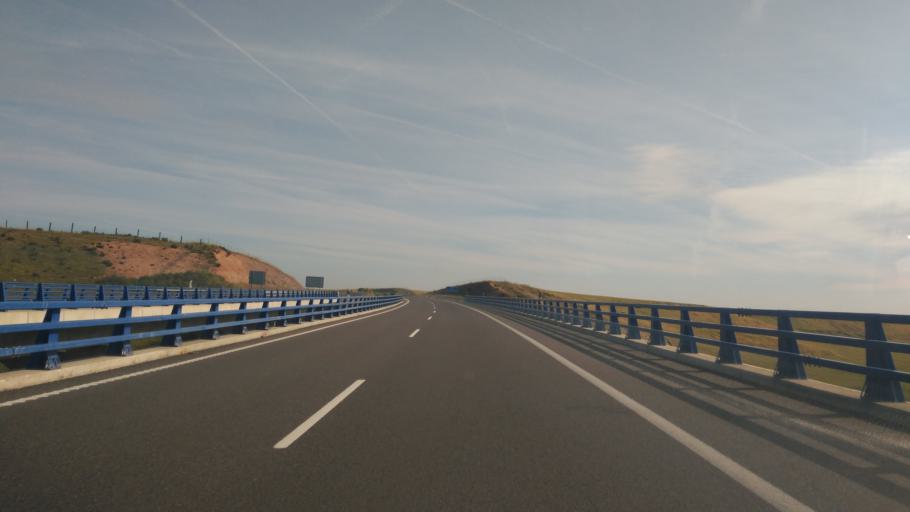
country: ES
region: Castille and Leon
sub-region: Provincia de Salamanca
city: Monterrubio de Armuna
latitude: 41.0399
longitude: -5.6674
